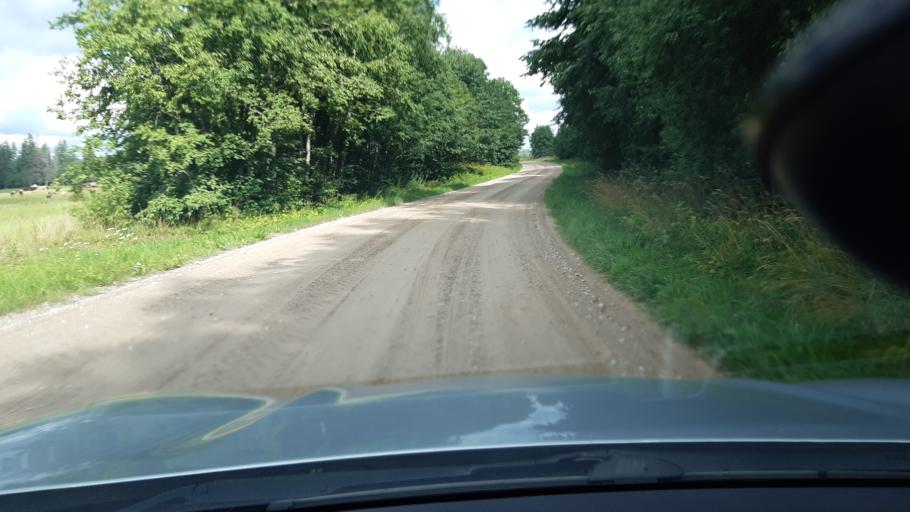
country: EE
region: Jaervamaa
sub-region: Tueri vald
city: Tueri
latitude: 58.9416
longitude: 25.2608
